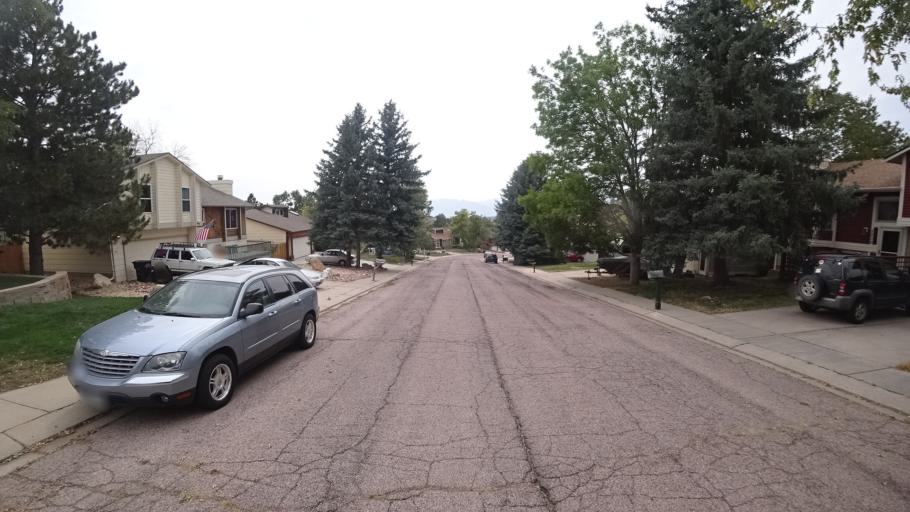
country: US
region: Colorado
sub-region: El Paso County
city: Cimarron Hills
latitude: 38.9047
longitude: -104.7262
